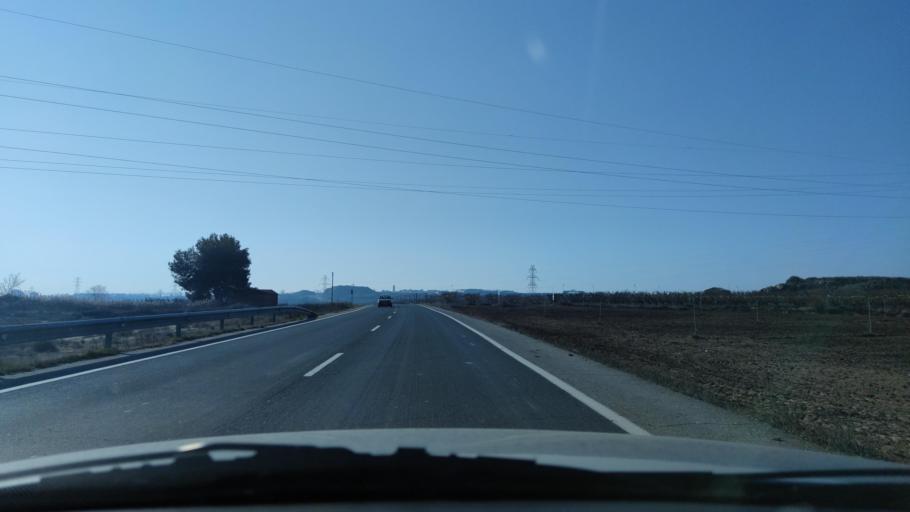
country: ES
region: Catalonia
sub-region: Provincia de Lleida
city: Albesa
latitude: 41.7101
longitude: 0.6385
